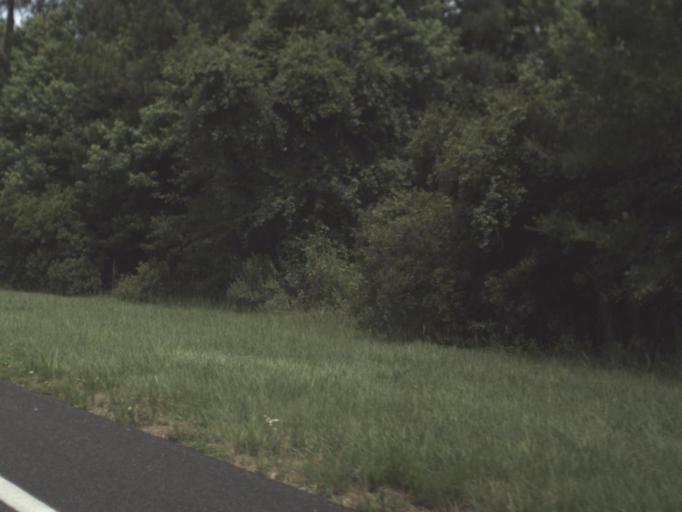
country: US
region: Florida
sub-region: Alachua County
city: Gainesville
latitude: 29.6065
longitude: -82.2237
